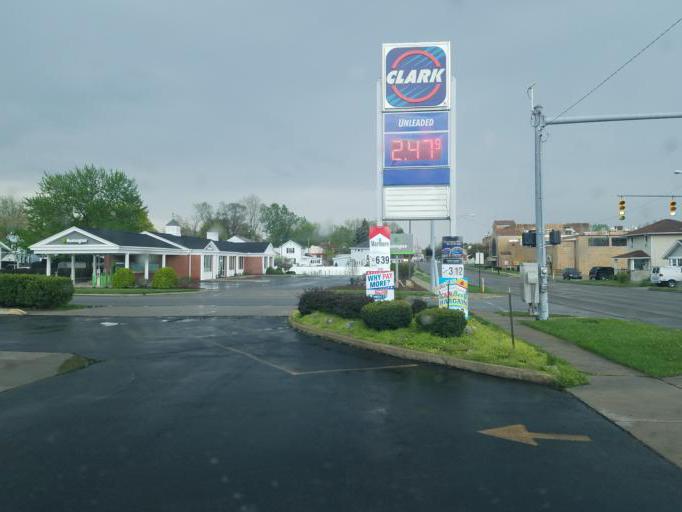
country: US
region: Ohio
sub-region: Seneca County
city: Fostoria
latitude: 41.1644
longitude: -83.4209
